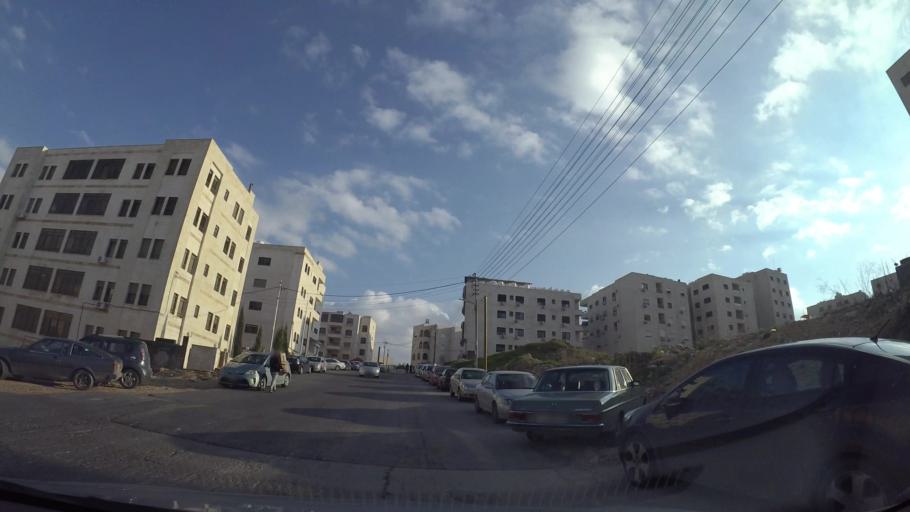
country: JO
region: Amman
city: Al Jubayhah
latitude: 32.0040
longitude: 35.8702
